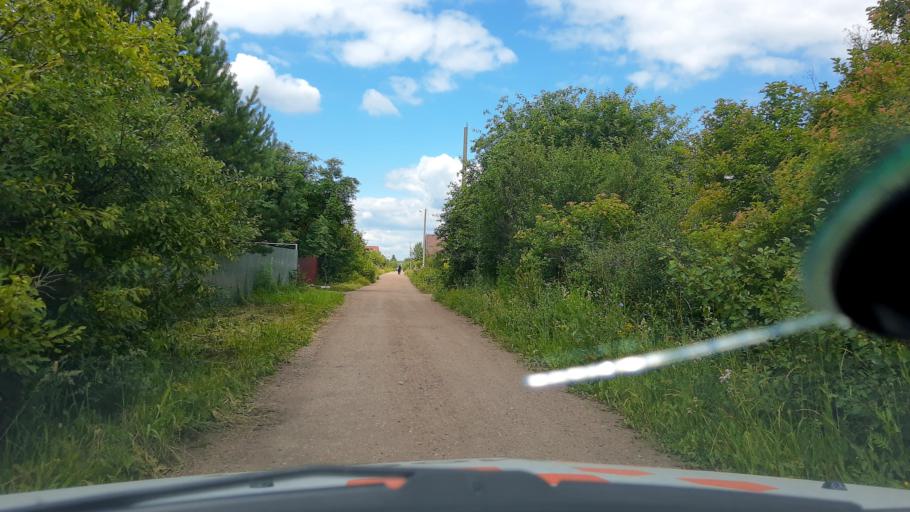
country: RU
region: Bashkortostan
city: Kabakovo
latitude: 54.7201
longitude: 56.2094
